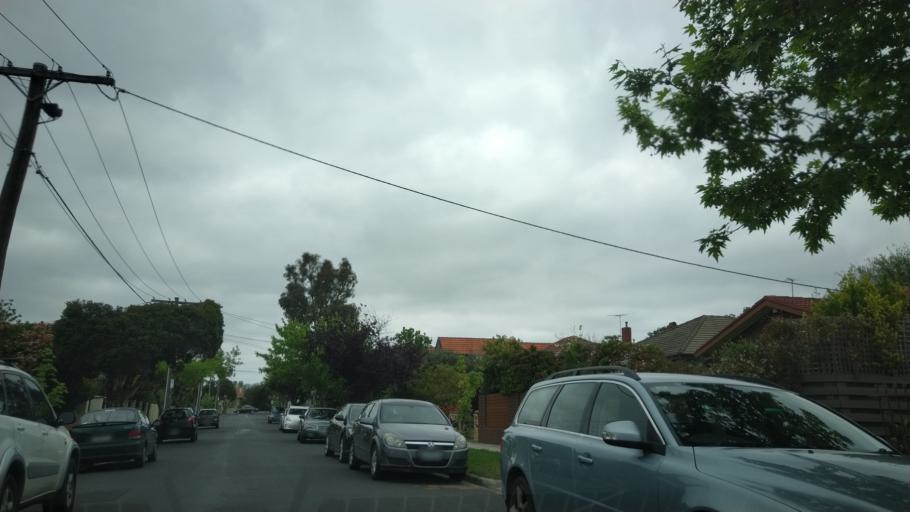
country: AU
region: Victoria
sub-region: Glen Eira
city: Murrumbeena
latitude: -37.8969
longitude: 145.0742
